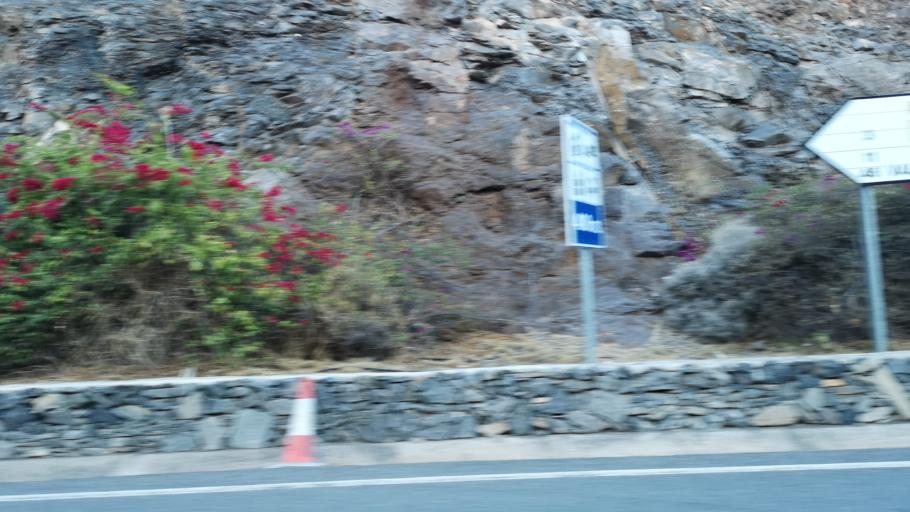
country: ES
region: Canary Islands
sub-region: Provincia de Santa Cruz de Tenerife
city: Alajero
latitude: 28.0334
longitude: -17.2017
